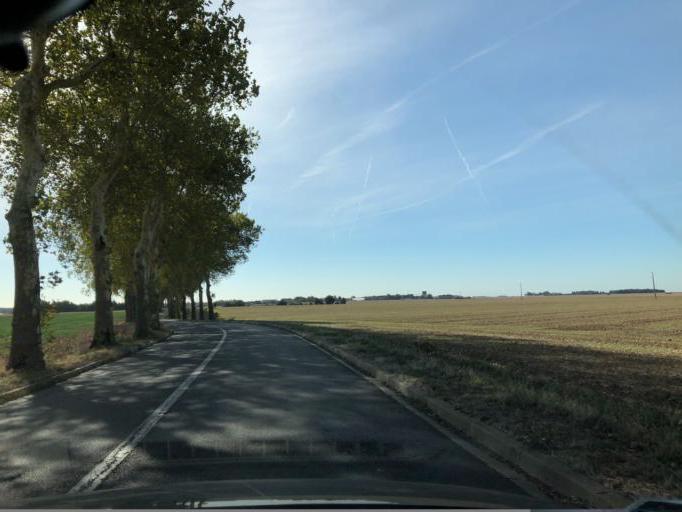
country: FR
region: Ile-de-France
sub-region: Departement de l'Essonne
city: Morigny-Champigny
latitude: 48.3817
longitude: 2.2313
